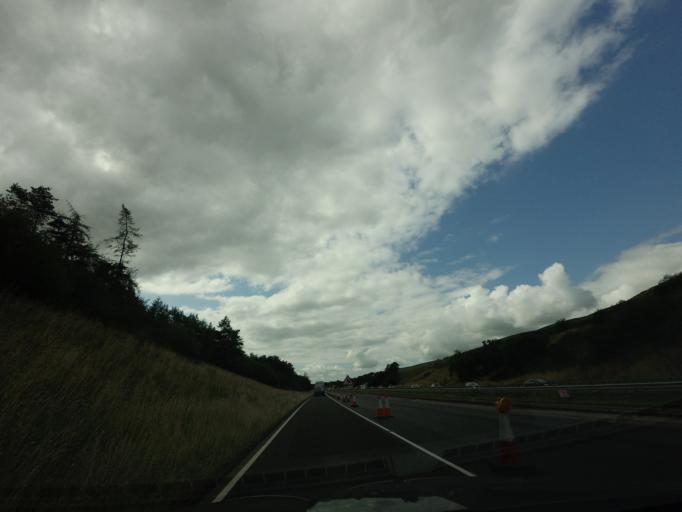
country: GB
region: England
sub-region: Cumbria
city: Kendal
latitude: 54.3142
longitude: -2.6393
